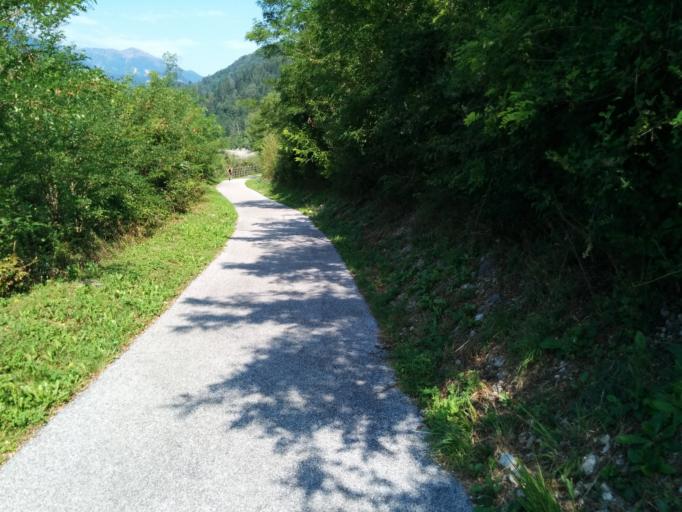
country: IT
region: Friuli Venezia Giulia
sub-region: Provincia di Udine
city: Villa Santina
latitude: 46.4240
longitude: 12.9050
